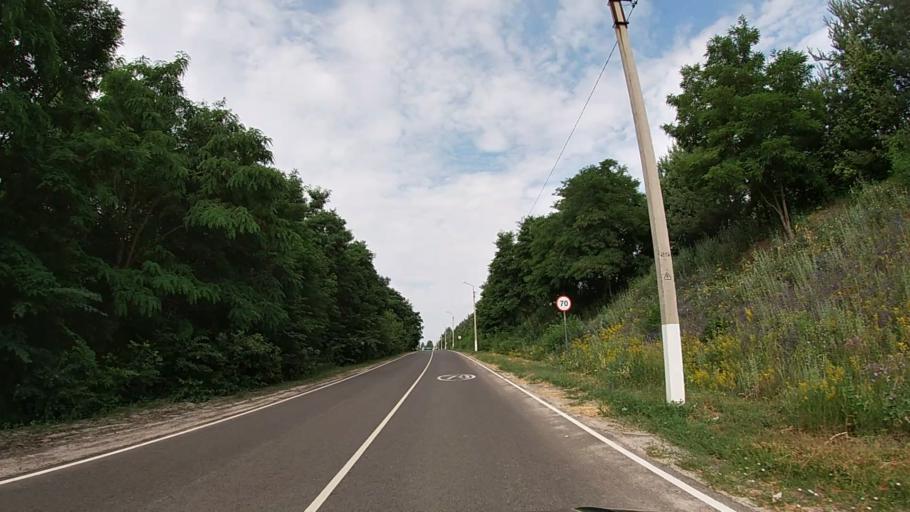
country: UA
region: Sumy
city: Krasnopillya
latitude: 50.8142
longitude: 35.4218
